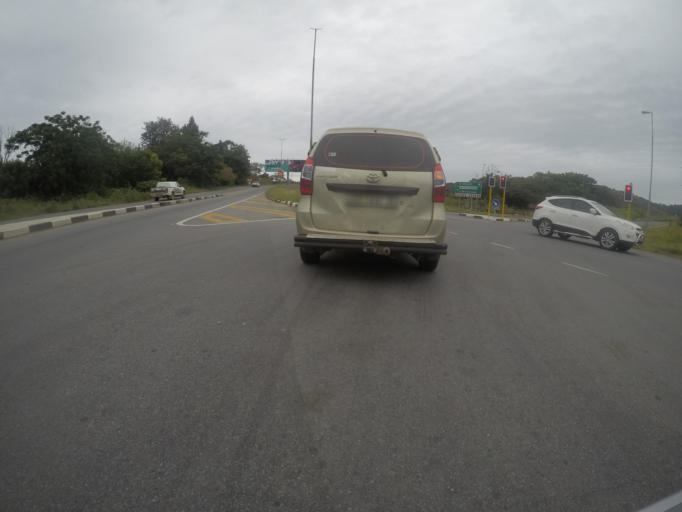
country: ZA
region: Eastern Cape
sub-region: Buffalo City Metropolitan Municipality
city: East London
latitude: -32.9642
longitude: 27.9201
